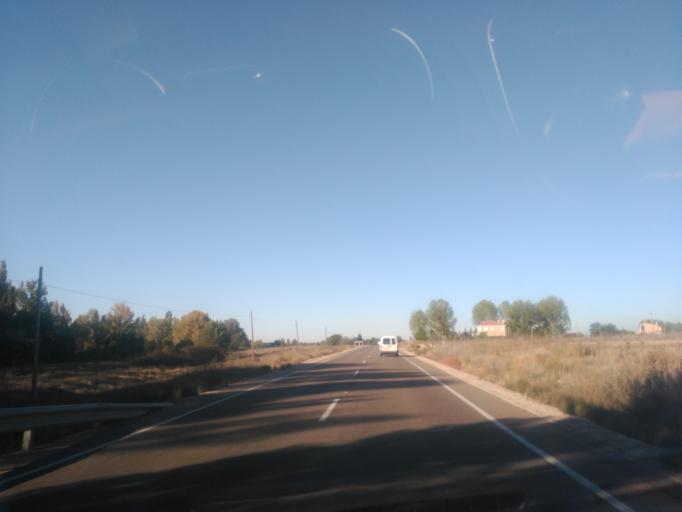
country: ES
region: Castille and Leon
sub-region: Provincia de Burgos
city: Quemada
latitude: 41.6876
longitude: -3.6173
